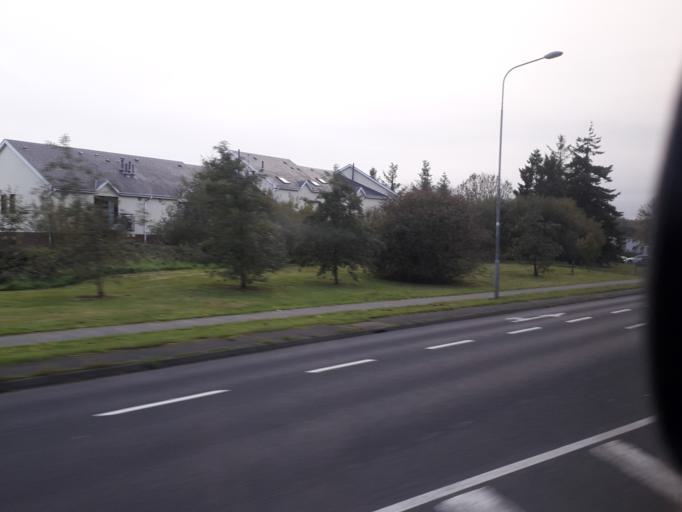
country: IE
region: Munster
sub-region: An Clar
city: Shannon
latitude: 52.7140
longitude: -8.8676
